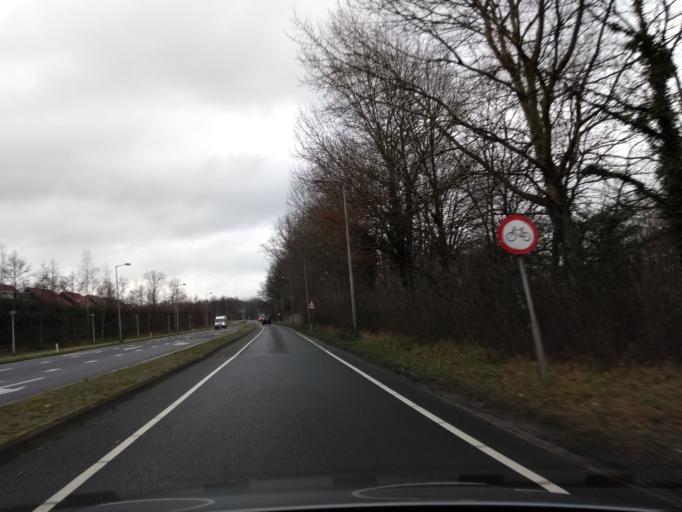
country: NL
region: Overijssel
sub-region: Gemeente Enschede
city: Enschede
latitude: 52.2177
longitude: 6.9393
